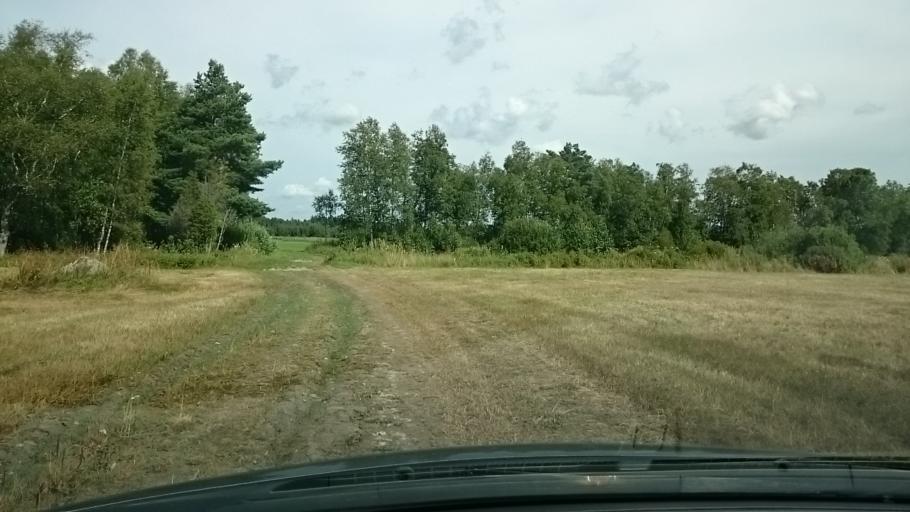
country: EE
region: Laeaene
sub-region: Ridala Parish
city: Uuemoisa
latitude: 59.0160
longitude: 23.5775
